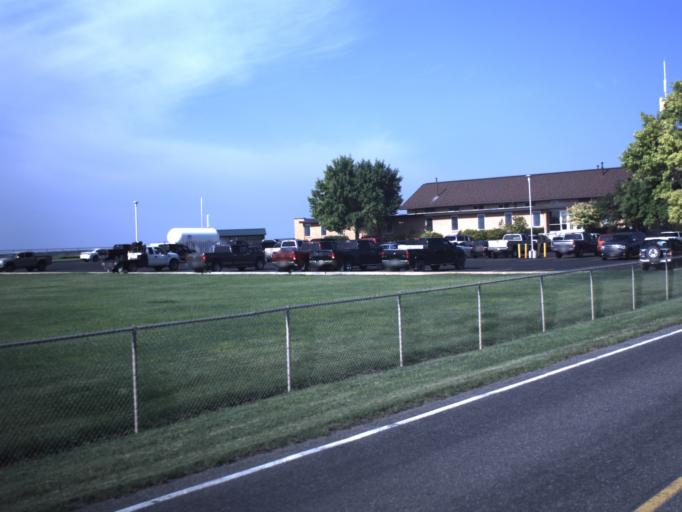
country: US
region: Utah
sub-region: Duchesne County
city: Duchesne
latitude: 40.3555
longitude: -110.3796
